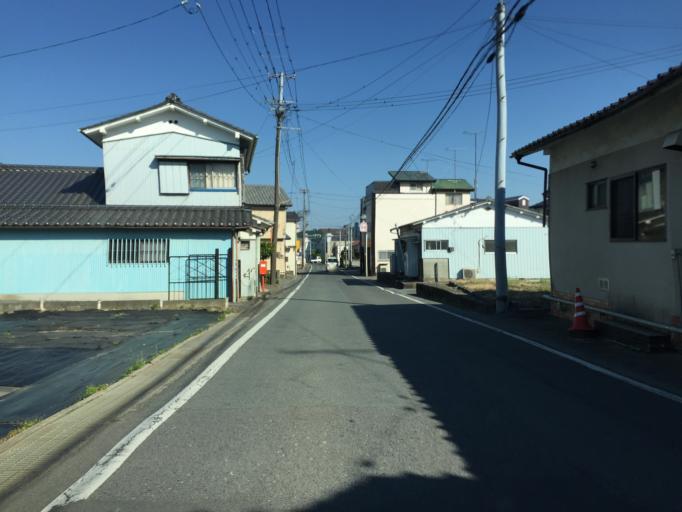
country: JP
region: Ibaraki
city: Kitaibaraki
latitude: 36.8932
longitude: 140.7559
